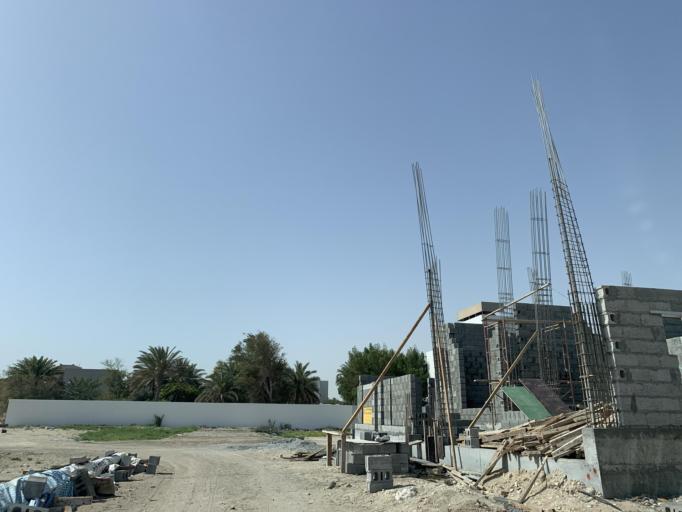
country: BH
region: Northern
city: Sitrah
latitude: 26.1477
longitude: 50.6059
